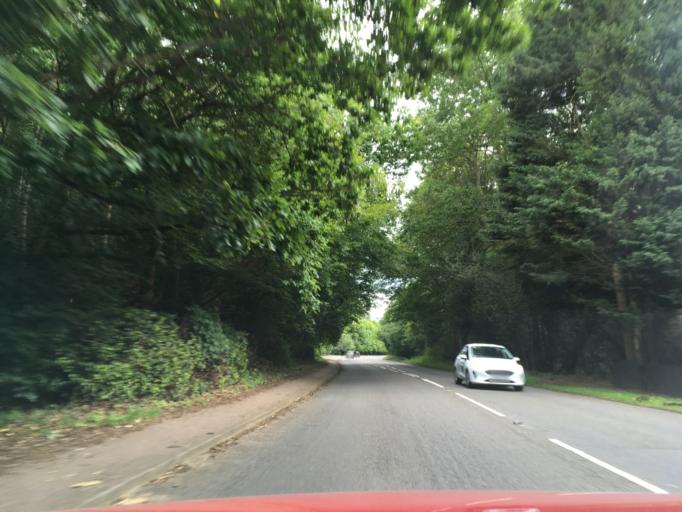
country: GB
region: England
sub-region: Milton Keynes
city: Woburn Sands
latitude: 52.0078
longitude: -0.6445
